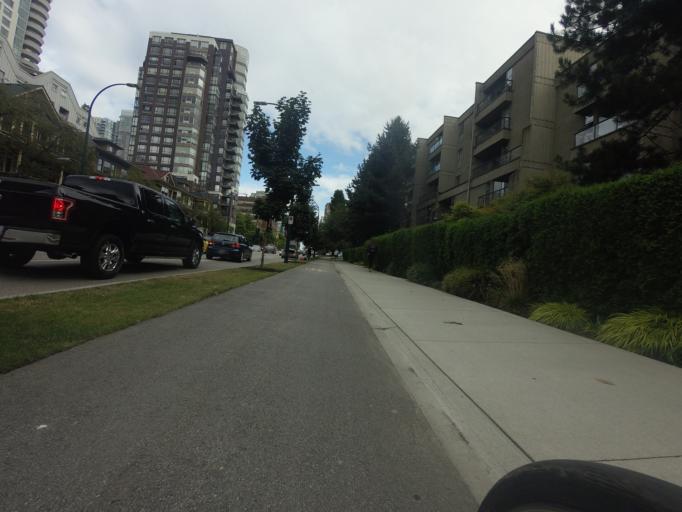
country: CA
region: British Columbia
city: West End
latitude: 49.2777
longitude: -123.1336
